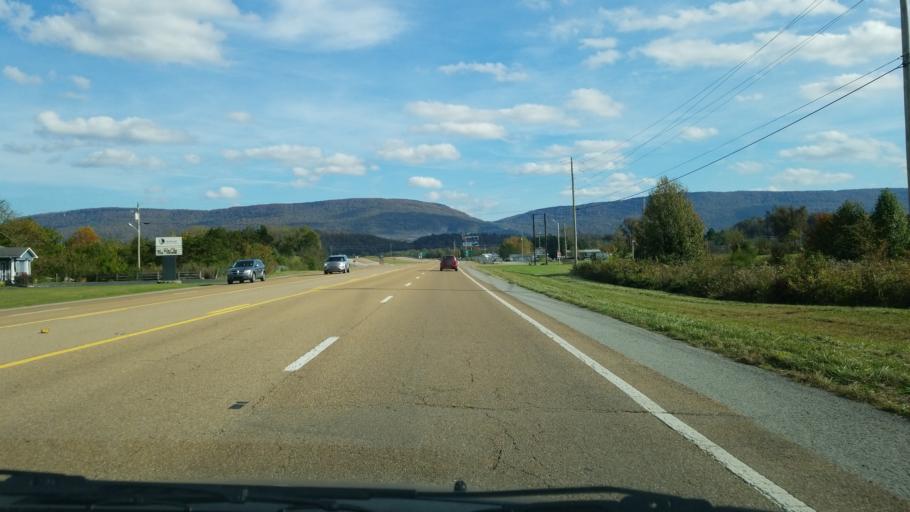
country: US
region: Tennessee
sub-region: Sequatchie County
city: Dunlap
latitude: 35.3980
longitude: -85.3800
